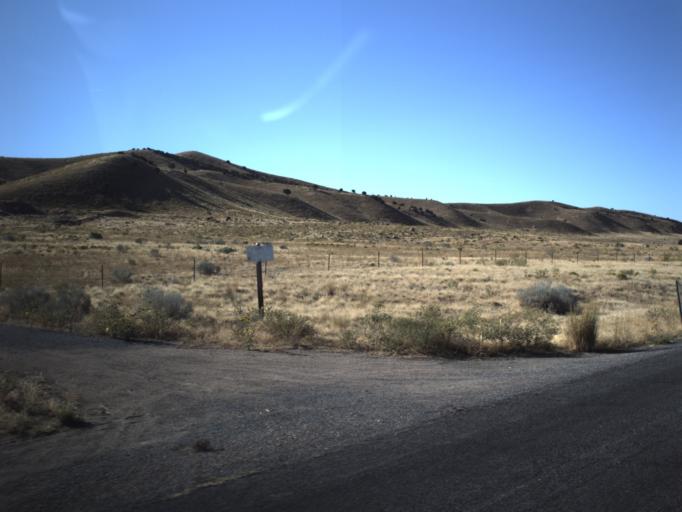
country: US
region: Utah
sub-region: Millard County
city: Delta
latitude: 39.4498
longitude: -112.3075
